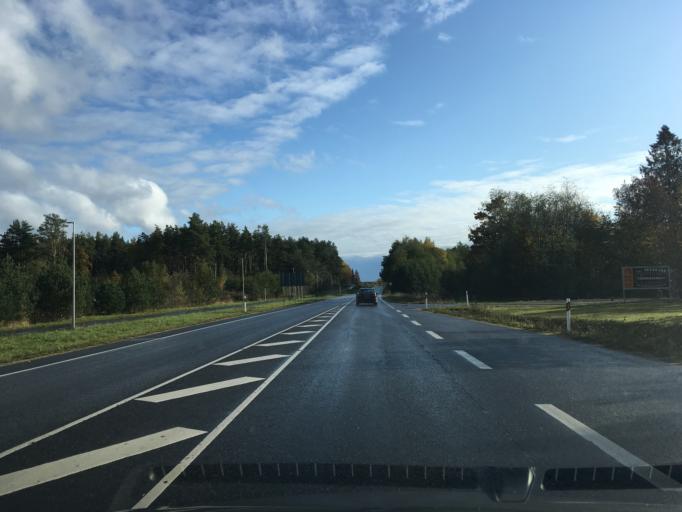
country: EE
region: Harju
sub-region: Raasiku vald
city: Arukula
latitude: 59.1841
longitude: 25.1307
